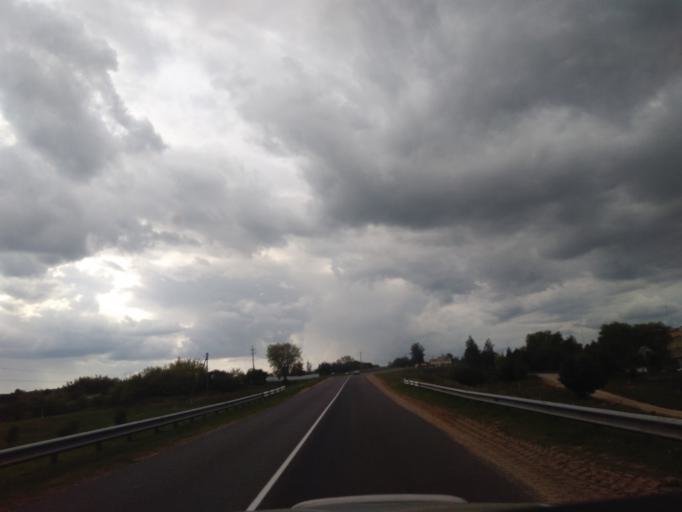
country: BY
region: Minsk
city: Kapyl'
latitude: 53.1450
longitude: 27.0778
